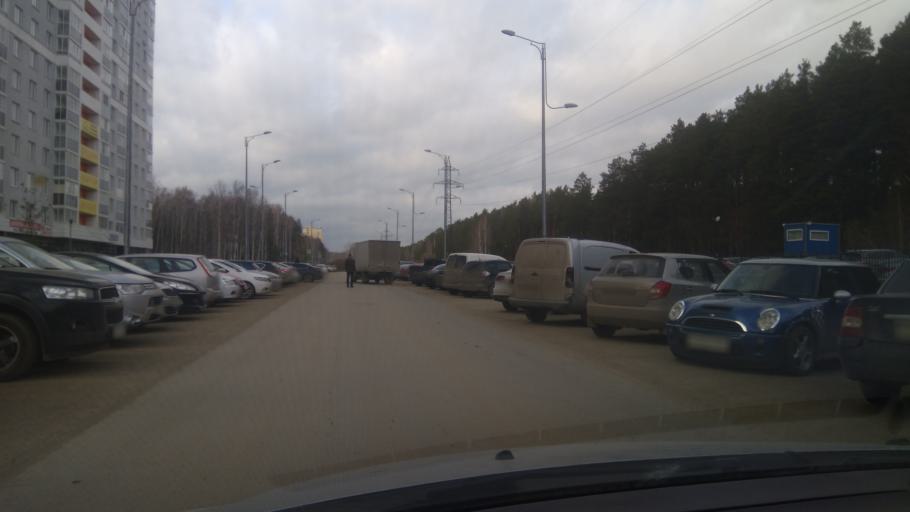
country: RU
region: Sverdlovsk
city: Sovkhoznyy
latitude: 56.7860
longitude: 60.5488
